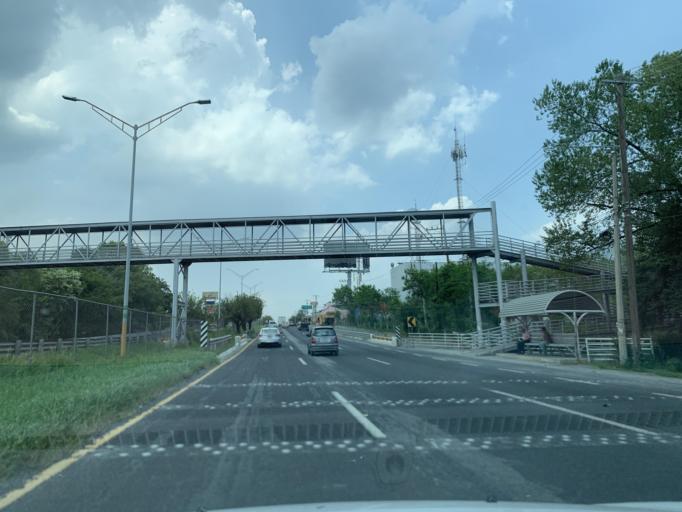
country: MX
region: Nuevo Leon
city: Santiago
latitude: 25.4933
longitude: -100.1869
